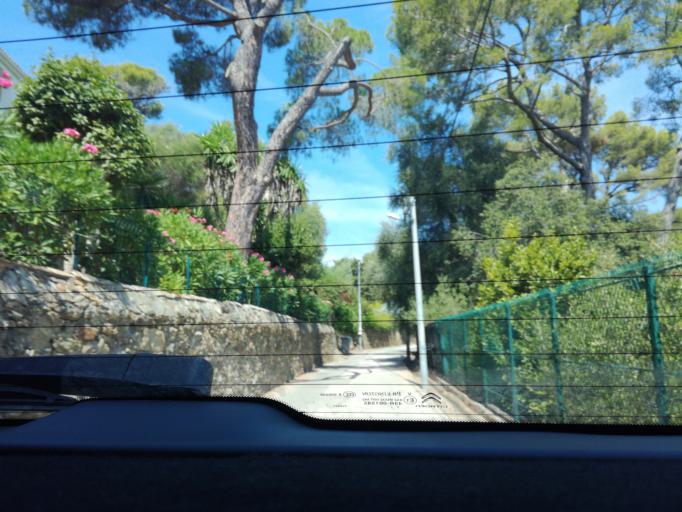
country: FR
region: Provence-Alpes-Cote d'Azur
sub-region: Departement du Var
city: Carqueiranne
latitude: 43.0364
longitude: 6.1302
